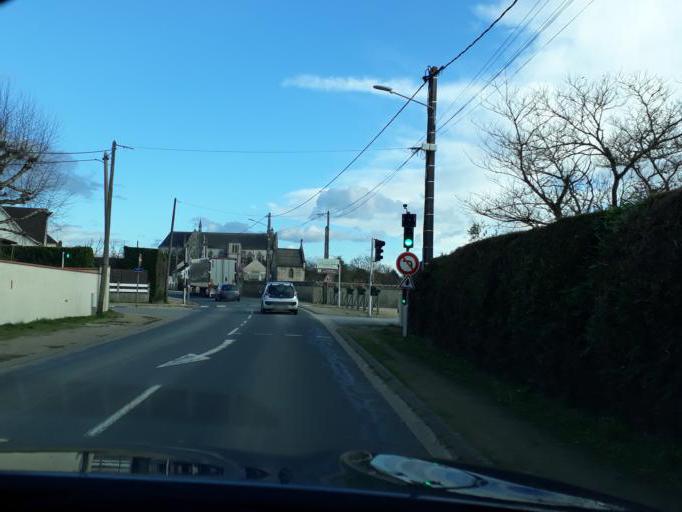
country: FR
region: Centre
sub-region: Departement du Loiret
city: Clery-Saint-Andre
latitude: 47.8225
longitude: 1.7505
